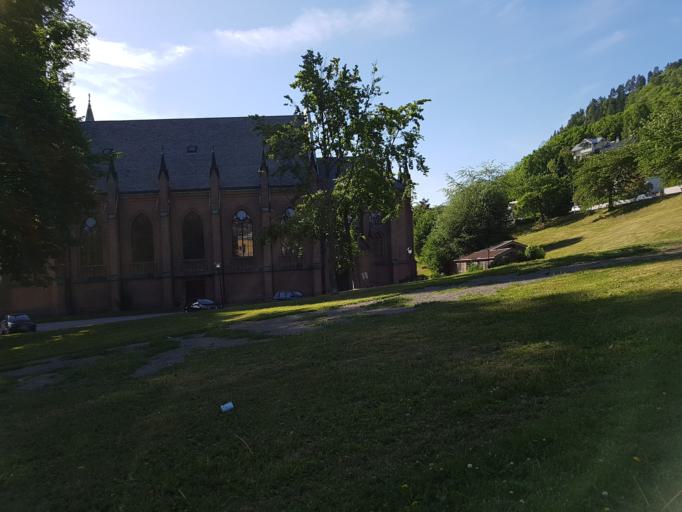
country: NO
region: Buskerud
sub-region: Drammen
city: Drammen
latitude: 59.7465
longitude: 10.2078
